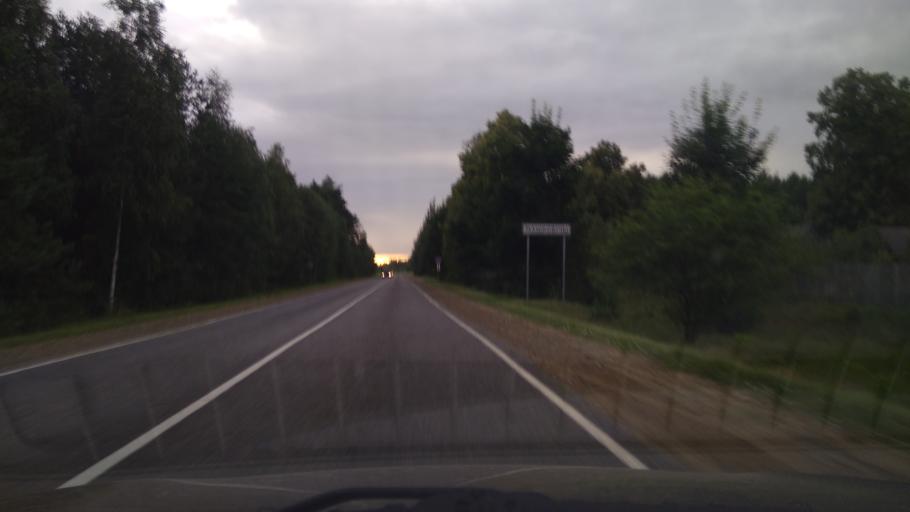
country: BY
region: Brest
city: Byaroza
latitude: 52.4148
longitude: 24.9860
